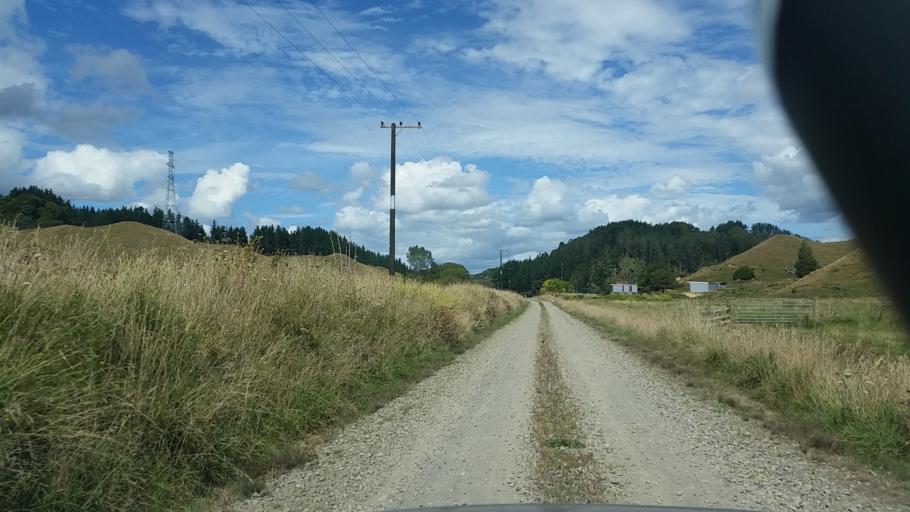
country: NZ
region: Taranaki
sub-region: South Taranaki District
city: Eltham
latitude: -39.2280
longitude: 174.5645
